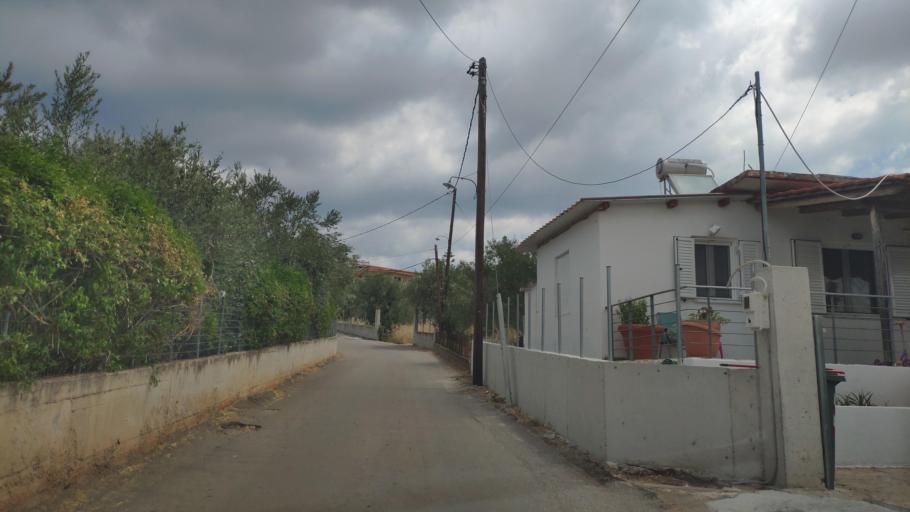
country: GR
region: Central Greece
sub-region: Nomos Fthiotidos
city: Malesina
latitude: 38.6639
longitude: 23.1812
